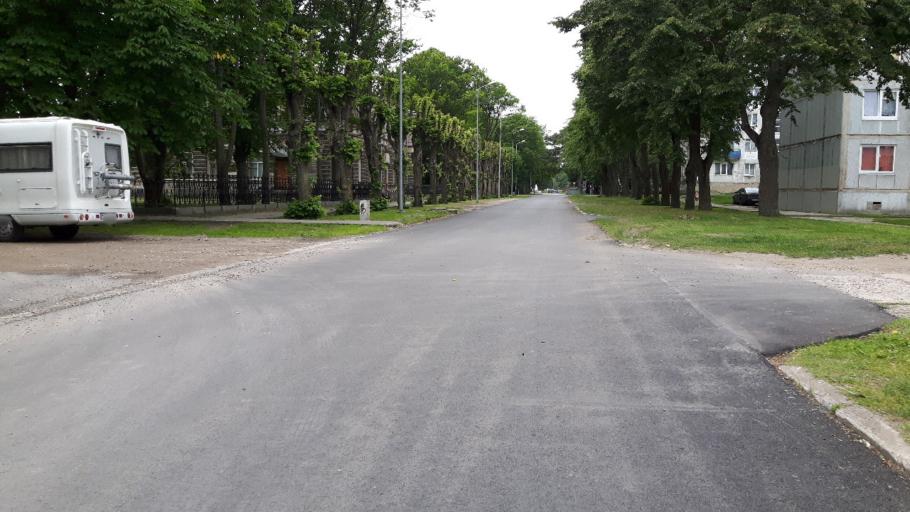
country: LV
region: Liepaja
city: Vec-Liepaja
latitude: 56.5530
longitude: 21.0096
